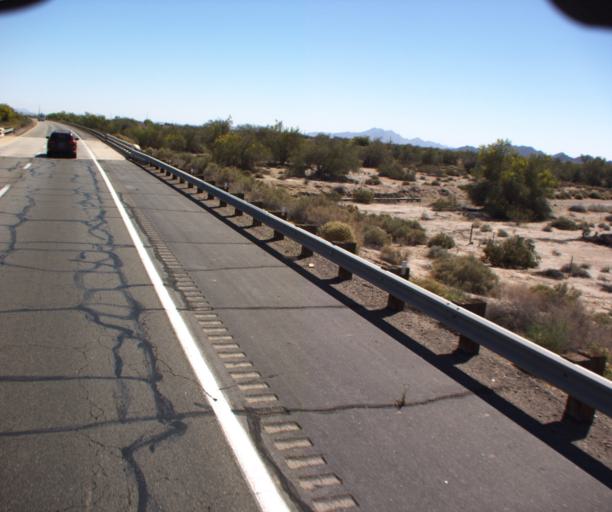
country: US
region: Arizona
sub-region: Yuma County
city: Wellton
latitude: 32.6491
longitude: -114.2109
